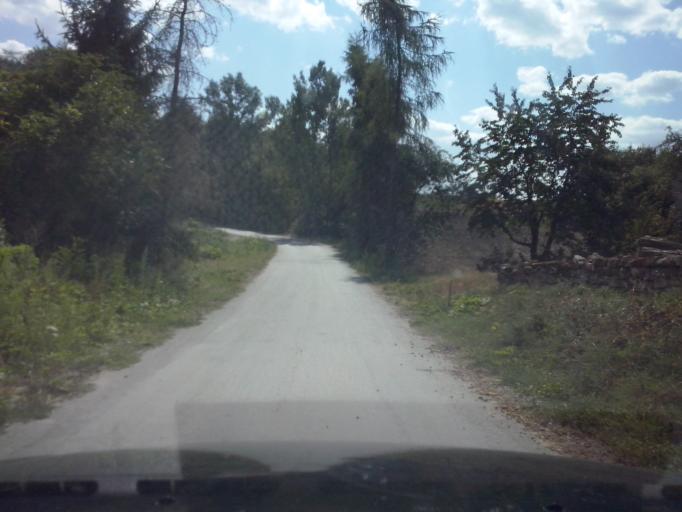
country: PL
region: Swietokrzyskie
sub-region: Powiat staszowski
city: Szydlow
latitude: 50.6063
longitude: 21.0682
